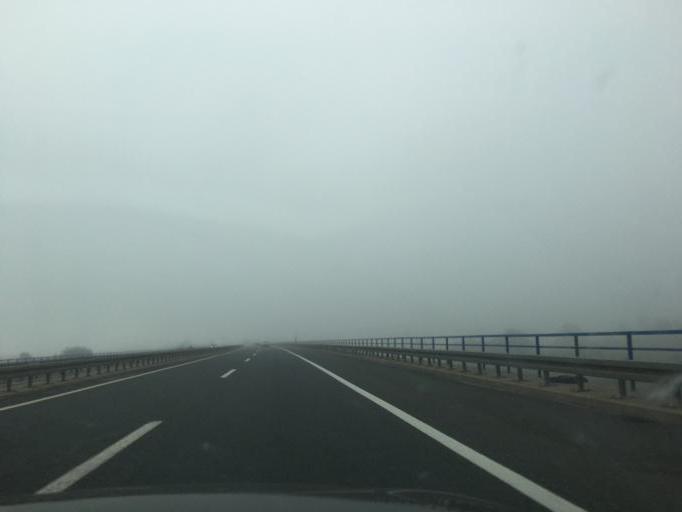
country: HR
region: Licko-Senjska
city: Gospic
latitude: 44.5688
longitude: 15.4265
